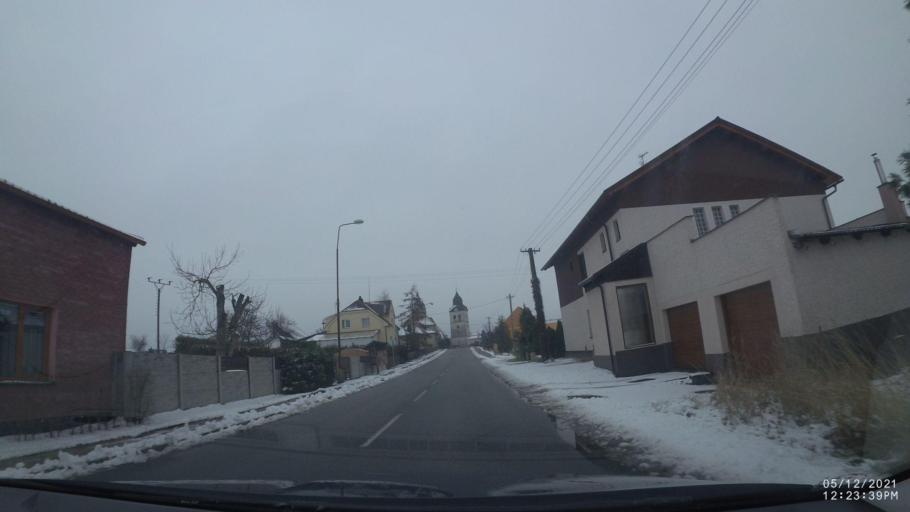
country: CZ
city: Ceske Mezirici
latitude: 50.3125
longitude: 16.0838
